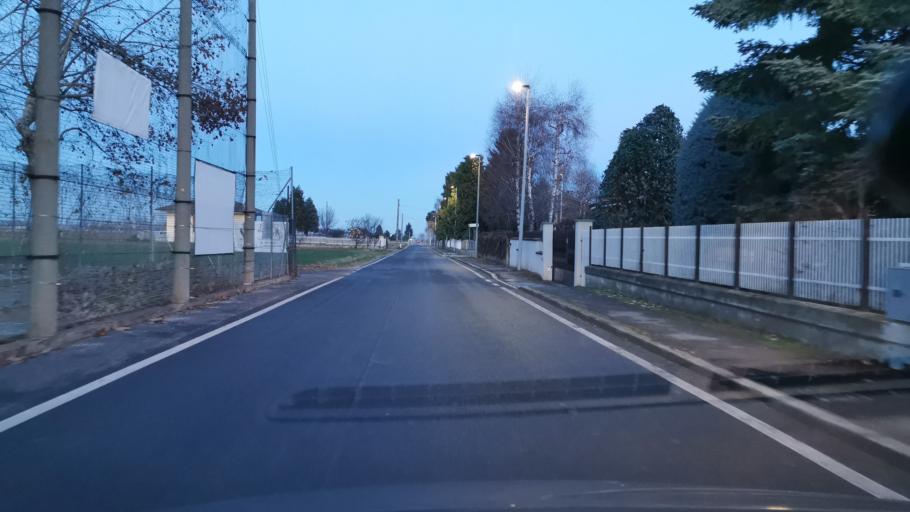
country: IT
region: Piedmont
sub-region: Provincia di Cuneo
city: Roata Rossi
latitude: 44.4541
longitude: 7.4911
